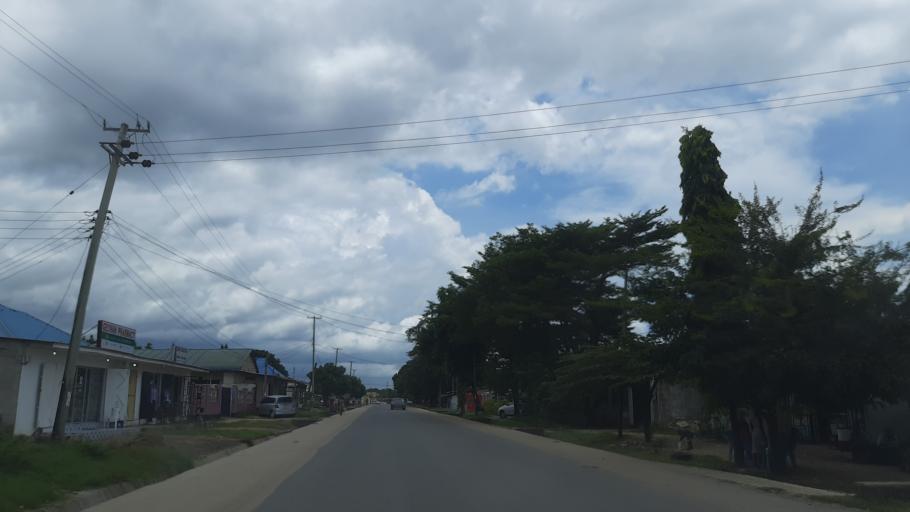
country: TZ
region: Dar es Salaam
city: Magomeni
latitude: -6.7774
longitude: 39.2357
